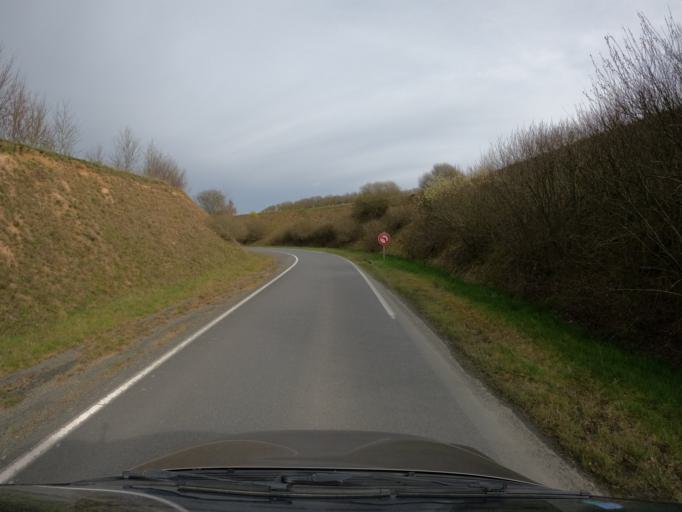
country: FR
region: Pays de la Loire
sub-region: Departement de la Vendee
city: Bouffere
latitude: 46.9602
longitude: -1.3201
